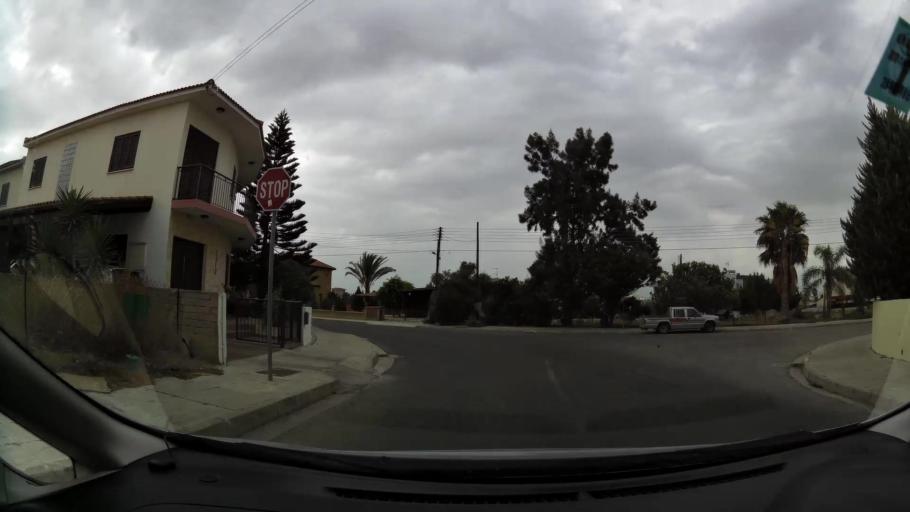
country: CY
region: Lefkosia
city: Geri
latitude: 35.1079
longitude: 33.3892
